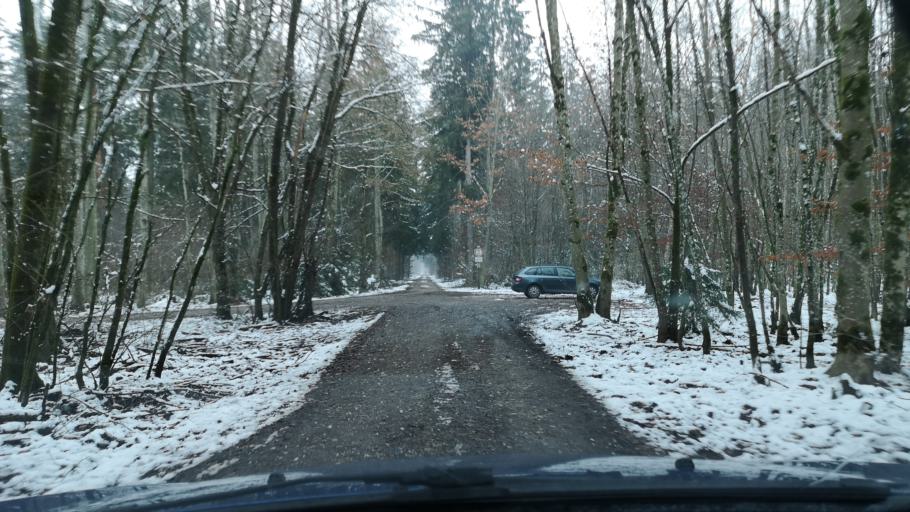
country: DE
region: Bavaria
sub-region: Upper Bavaria
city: Anzing
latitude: 48.1378
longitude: 11.8708
